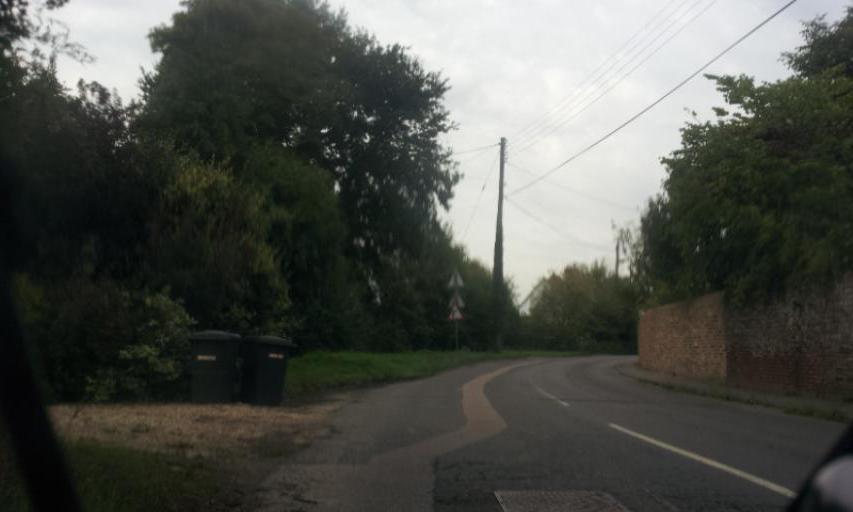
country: GB
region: England
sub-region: Kent
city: East Peckham
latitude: 51.2089
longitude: 0.3716
